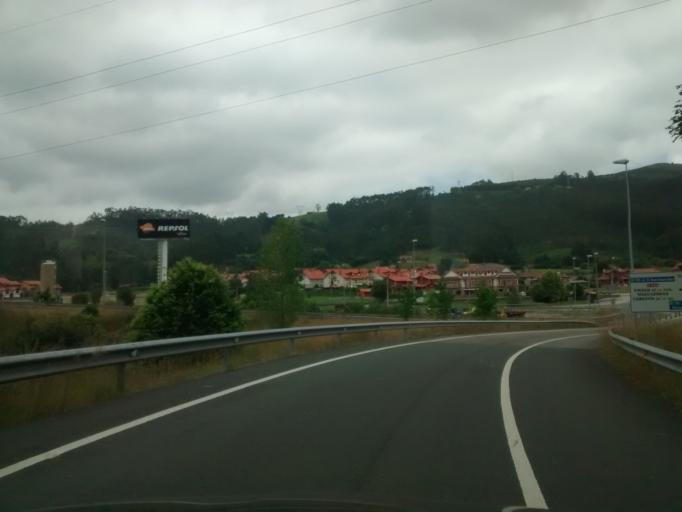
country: ES
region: Cantabria
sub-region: Provincia de Cantabria
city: Luzmela
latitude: 43.3266
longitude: -4.1904
